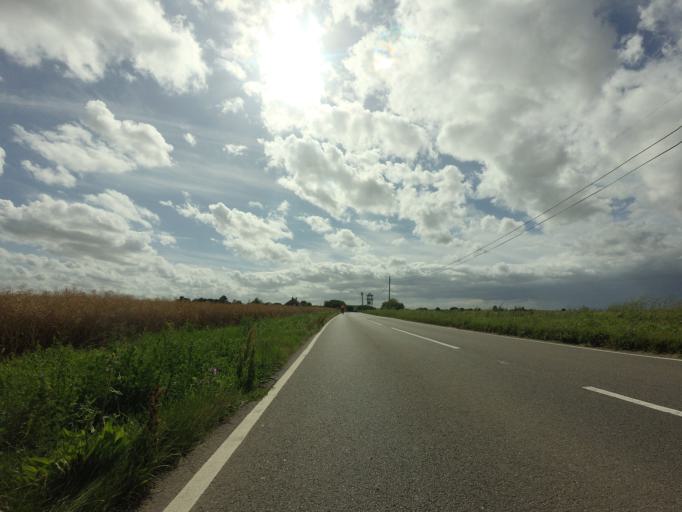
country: GB
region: England
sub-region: Medway
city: Allhallows
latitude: 51.4678
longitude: 0.6336
